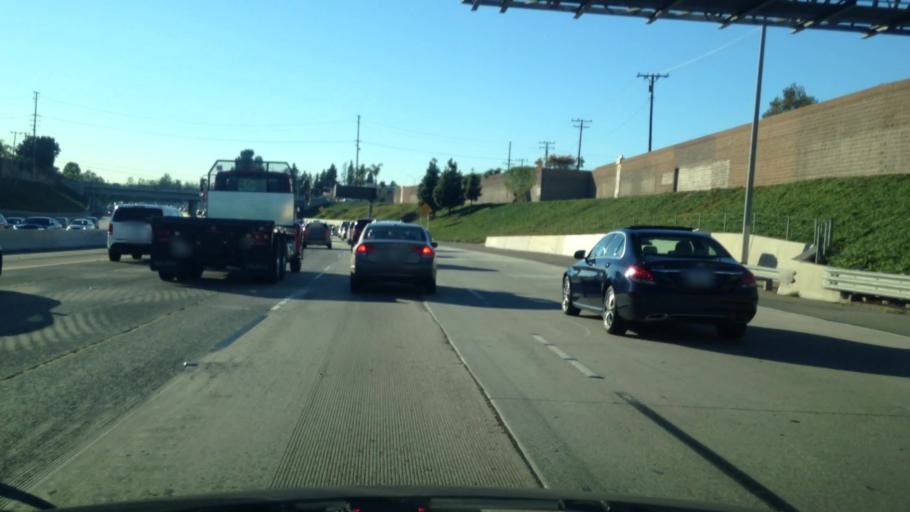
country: US
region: California
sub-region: Orange County
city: Orange
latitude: 33.7767
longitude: -117.8415
